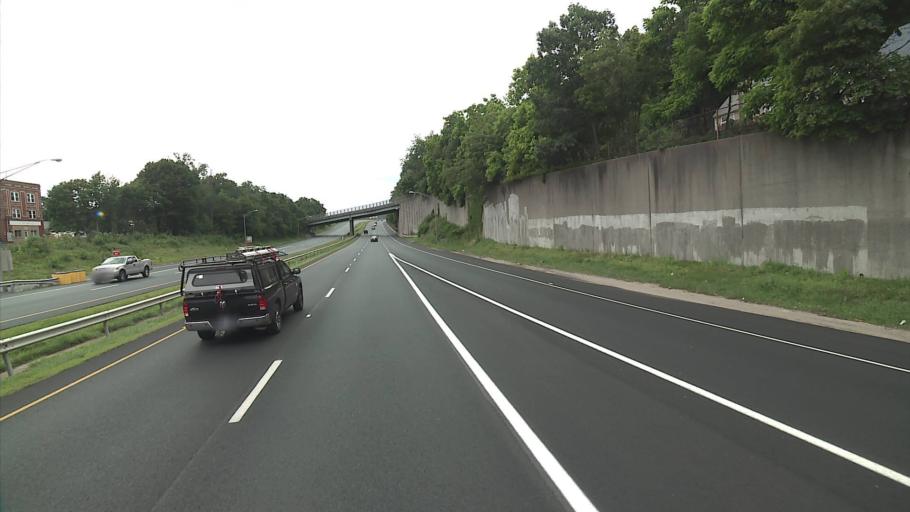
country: US
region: Connecticut
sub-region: New Haven County
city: Waterbury
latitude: 41.5388
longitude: -73.0443
